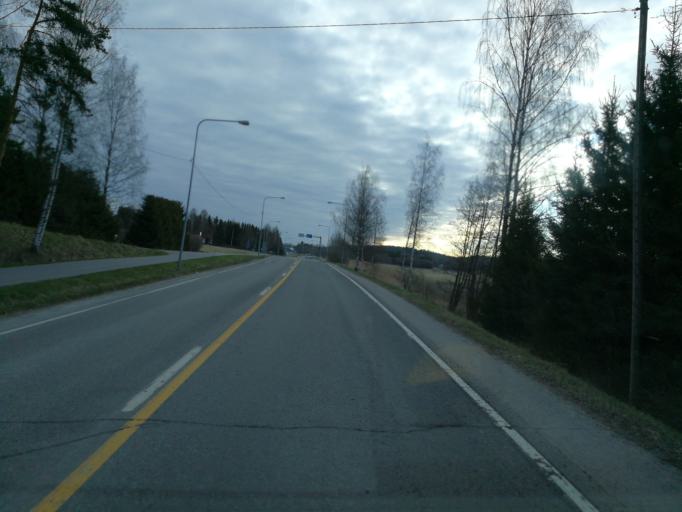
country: FI
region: Varsinais-Suomi
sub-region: Turku
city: Piikkioe
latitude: 60.4205
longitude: 22.4954
